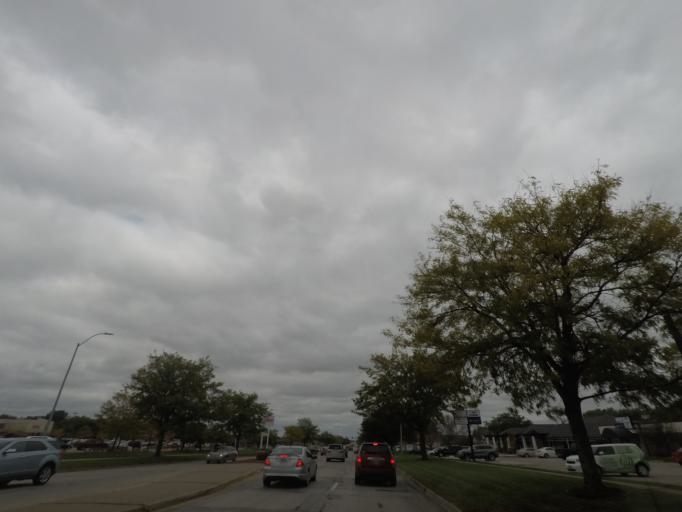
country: US
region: Iowa
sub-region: Polk County
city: Ankeny
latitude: 41.7334
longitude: -93.6003
